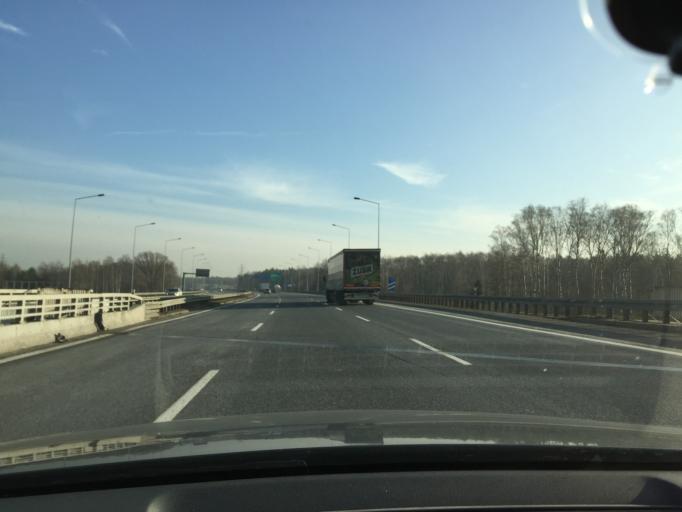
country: PL
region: Silesian Voivodeship
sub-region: Powiat gliwicki
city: Paniowki
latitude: 50.2633
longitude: 18.7846
